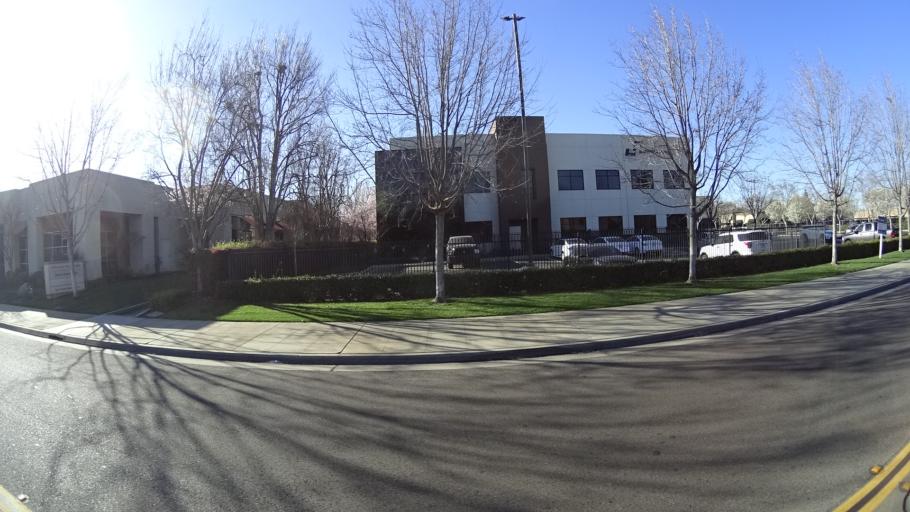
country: US
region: California
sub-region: Fresno County
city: Clovis
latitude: 36.8392
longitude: -119.7501
